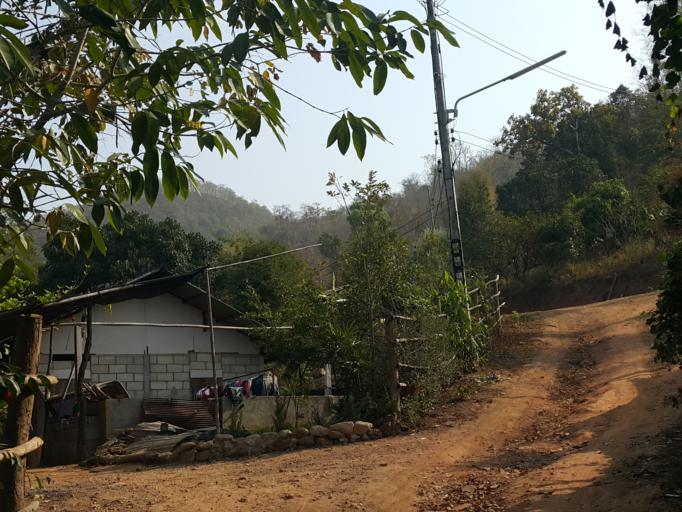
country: TH
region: Chiang Mai
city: Hang Dong
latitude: 18.7410
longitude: 98.8639
